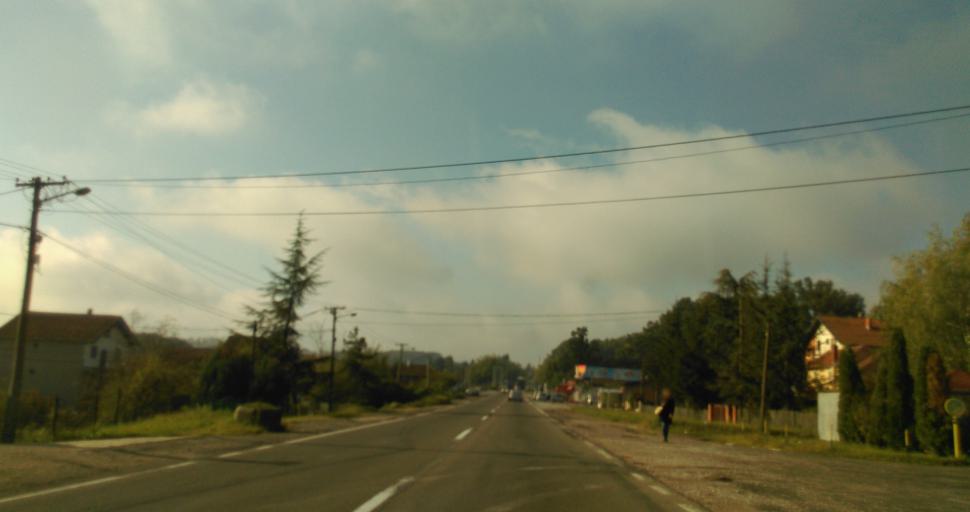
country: RS
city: Vranic
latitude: 44.6211
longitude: 20.3679
